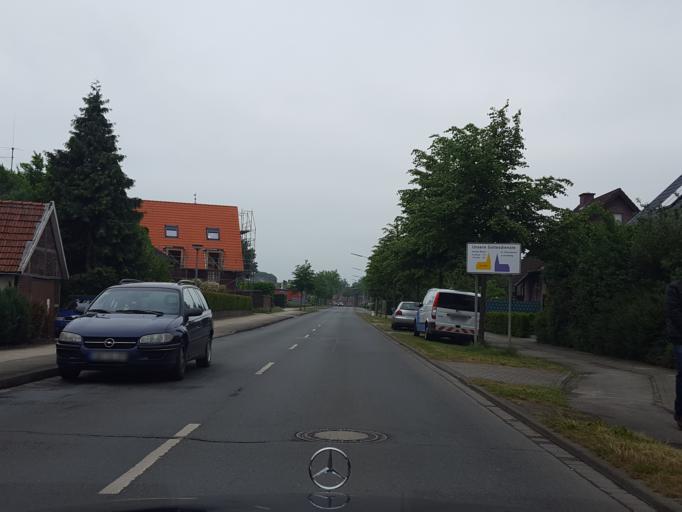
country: DE
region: North Rhine-Westphalia
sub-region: Regierungsbezirk Munster
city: Senden
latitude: 51.8204
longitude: 7.5503
